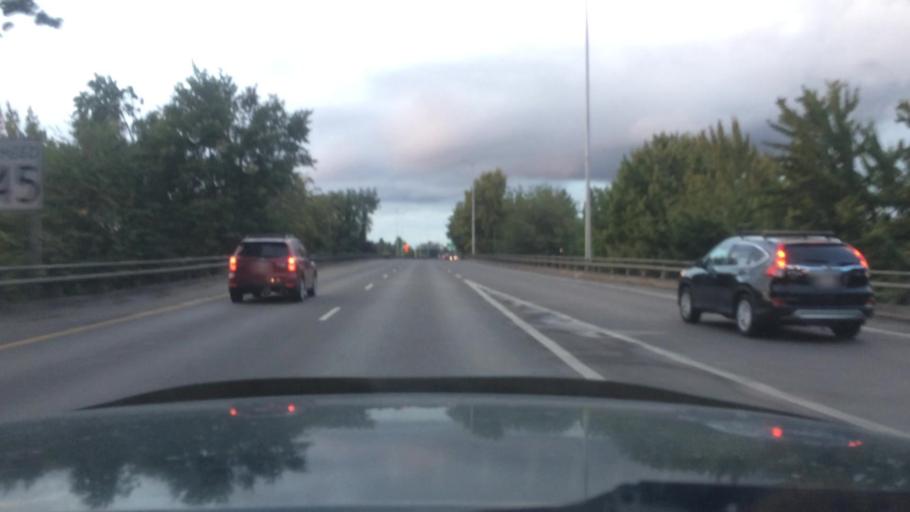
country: US
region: Oregon
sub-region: Lane County
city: Eugene
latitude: 44.0546
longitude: -123.1007
